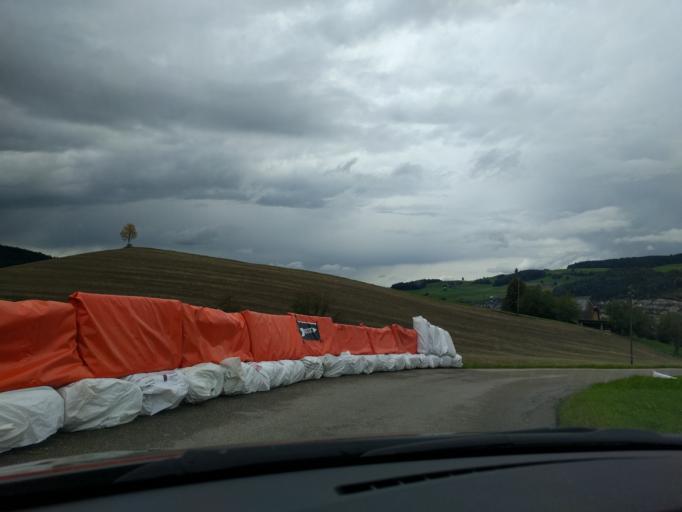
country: CH
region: Bern
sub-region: Bern-Mittelland District
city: Konolfingen
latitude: 46.8718
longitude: 7.6383
